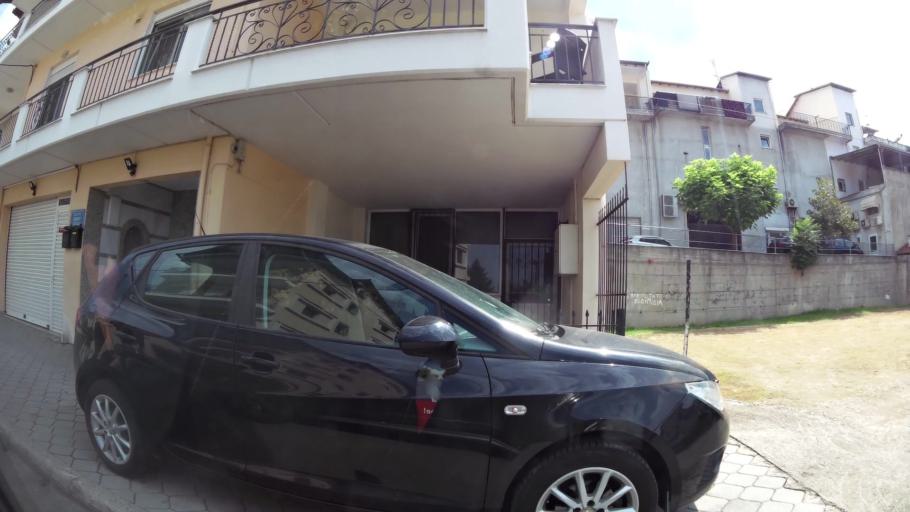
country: GR
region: Central Macedonia
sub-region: Nomos Imathias
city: Veroia
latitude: 40.5112
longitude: 22.2155
